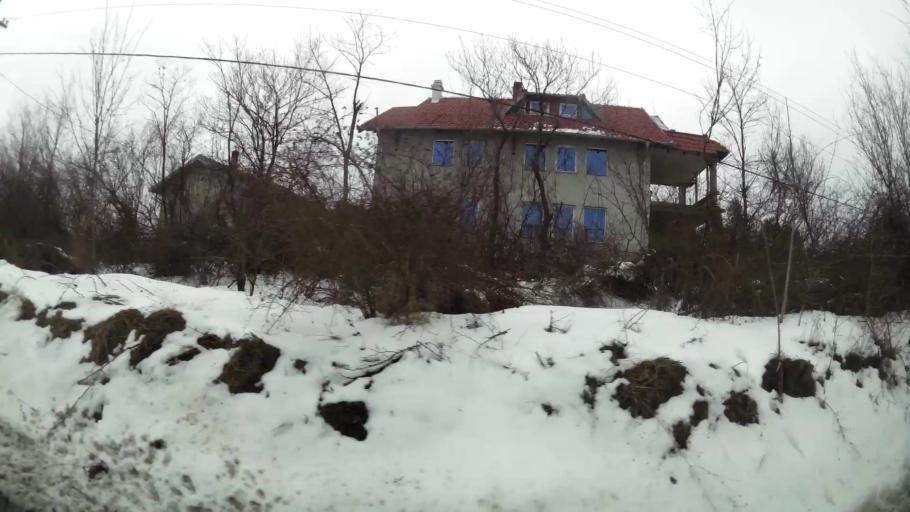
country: RS
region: Central Serbia
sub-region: Belgrade
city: Zvezdara
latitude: 44.7492
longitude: 20.5257
